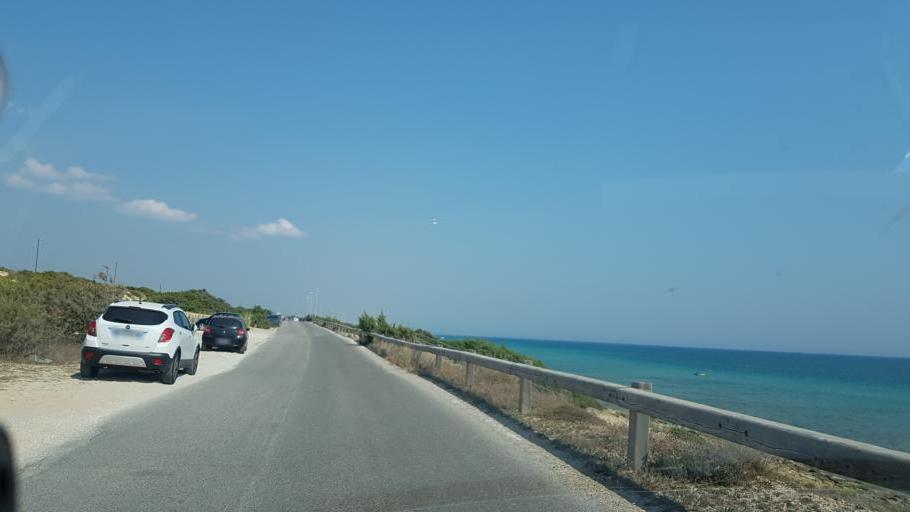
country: IT
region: Apulia
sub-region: Provincia di Taranto
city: Maruggio
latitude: 40.3000
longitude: 17.5975
